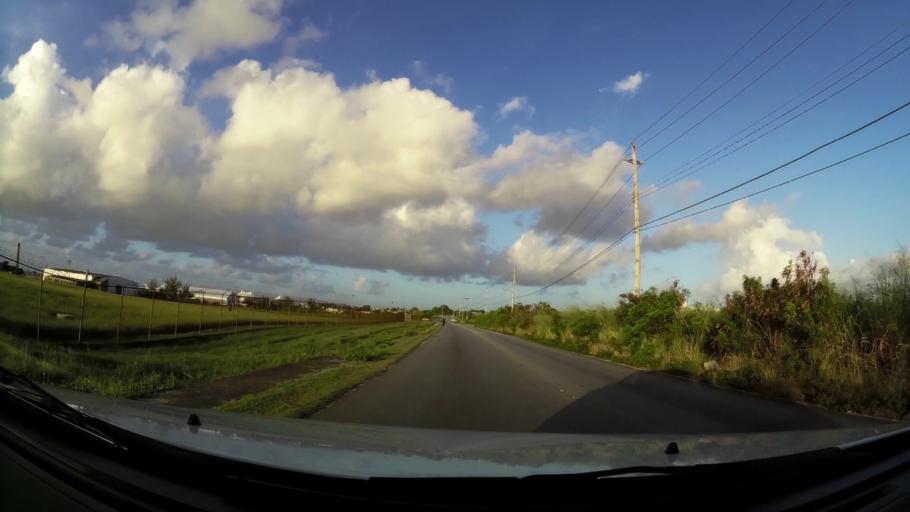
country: BB
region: Saint Philip
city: Crane
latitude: 13.0833
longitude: -59.4822
